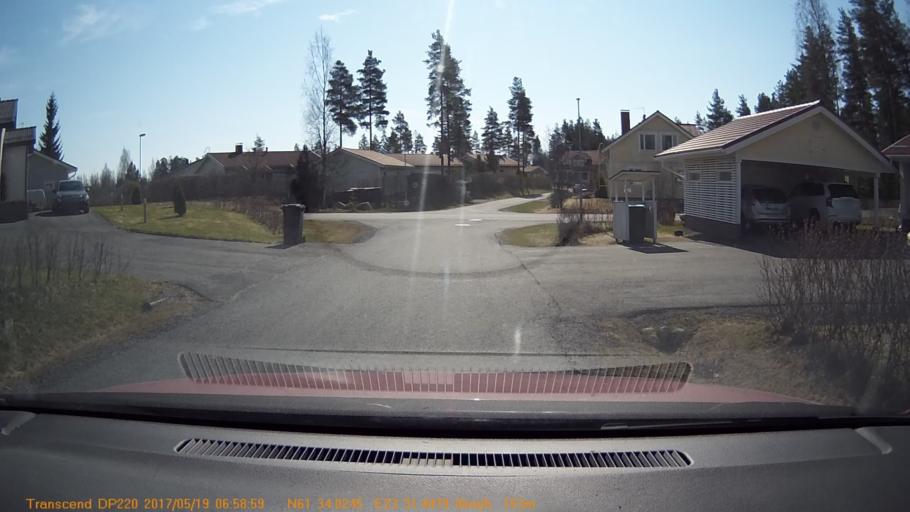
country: FI
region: Pirkanmaa
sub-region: Tampere
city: Yloejaervi
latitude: 61.5671
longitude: 23.5242
